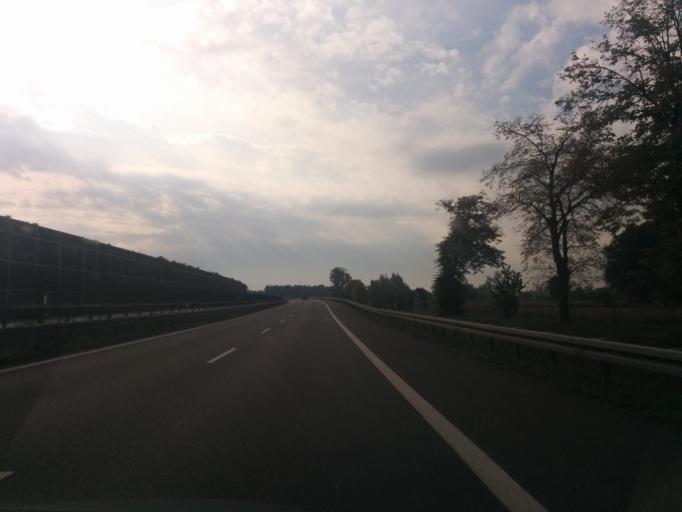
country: PL
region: Masovian Voivodeship
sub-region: Powiat bialobrzeski
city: Stara Blotnica
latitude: 51.5825
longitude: 21.0008
